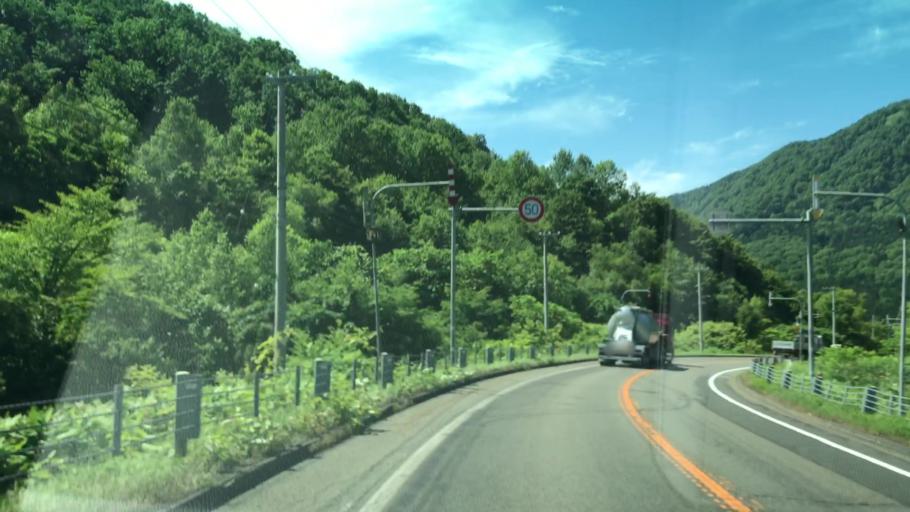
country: JP
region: Hokkaido
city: Shimo-furano
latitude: 42.8879
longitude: 142.4365
